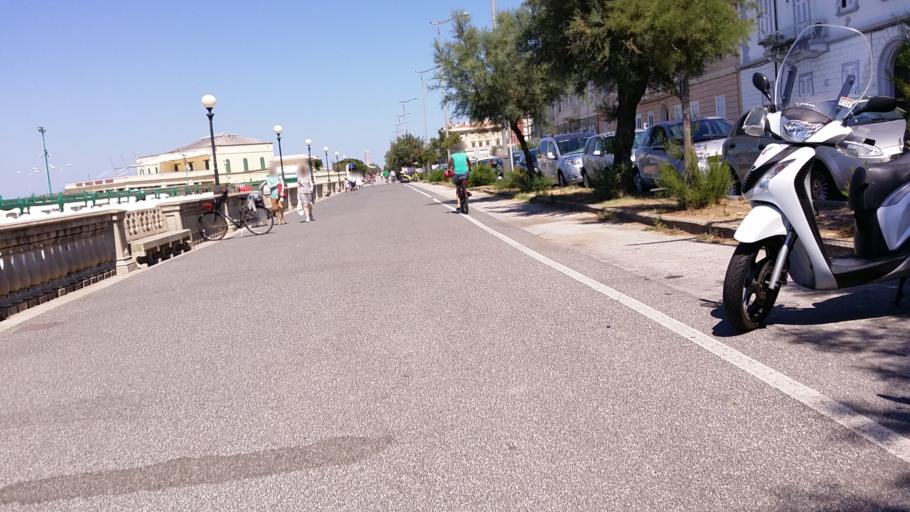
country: IT
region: Tuscany
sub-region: Provincia di Livorno
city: Livorno
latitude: 43.5310
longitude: 10.3034
